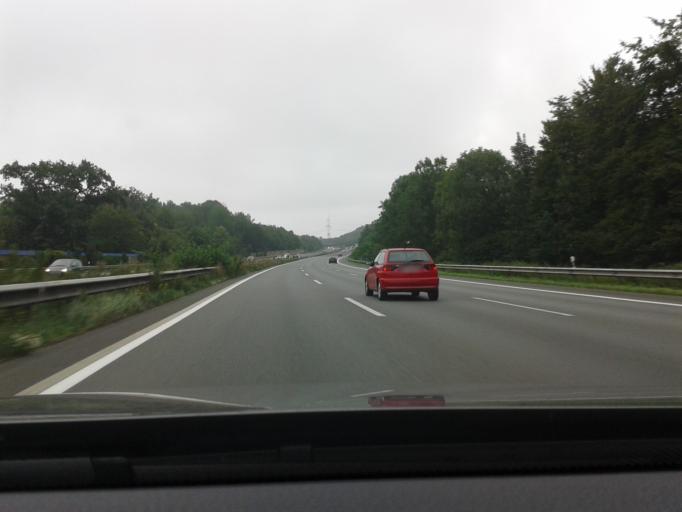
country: DE
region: North Rhine-Westphalia
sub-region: Regierungsbezirk Detmold
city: Leopoldshohe
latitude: 52.0358
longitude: 8.6418
